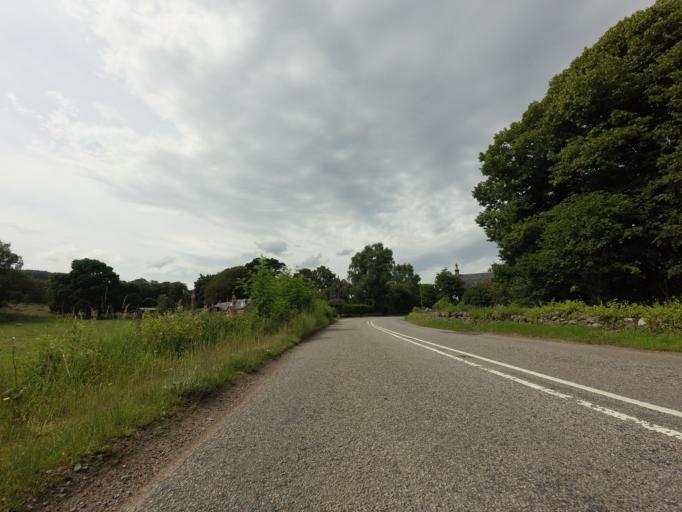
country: GB
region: Scotland
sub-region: Highland
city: Alness
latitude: 57.8563
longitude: -4.3110
